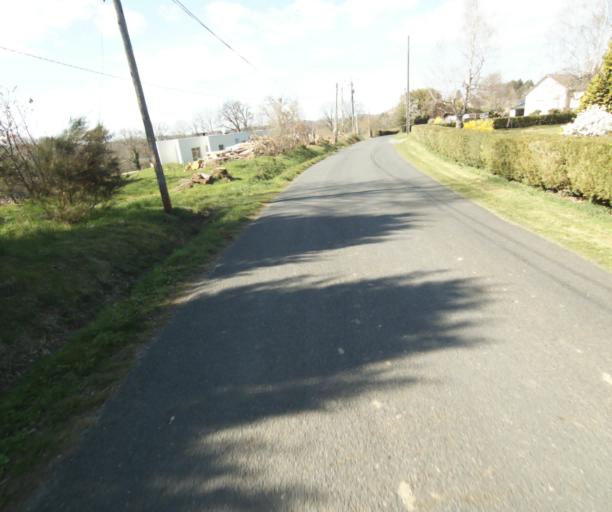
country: FR
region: Limousin
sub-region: Departement de la Correze
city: Saint-Mexant
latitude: 45.2939
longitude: 1.6496
